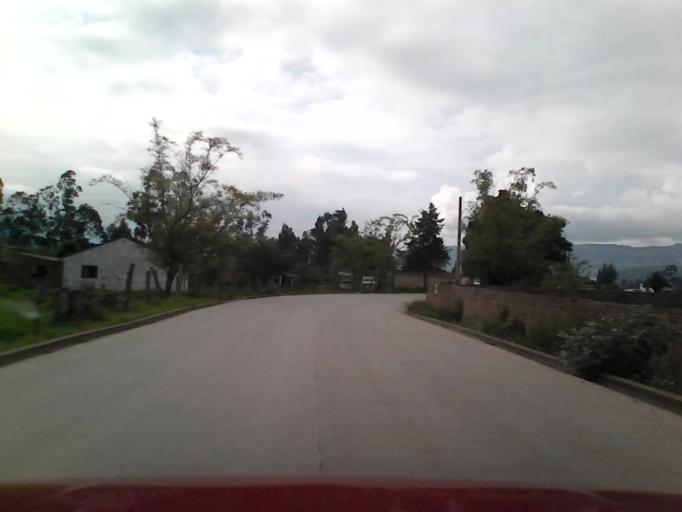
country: CO
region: Boyaca
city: Tibasosa
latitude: 5.7993
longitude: -72.9888
